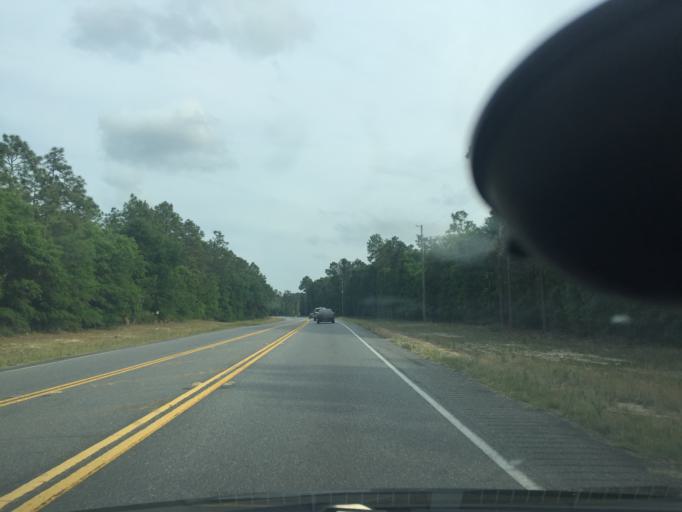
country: US
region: Georgia
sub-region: Chatham County
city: Bloomingdale
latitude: 32.0399
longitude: -81.3294
